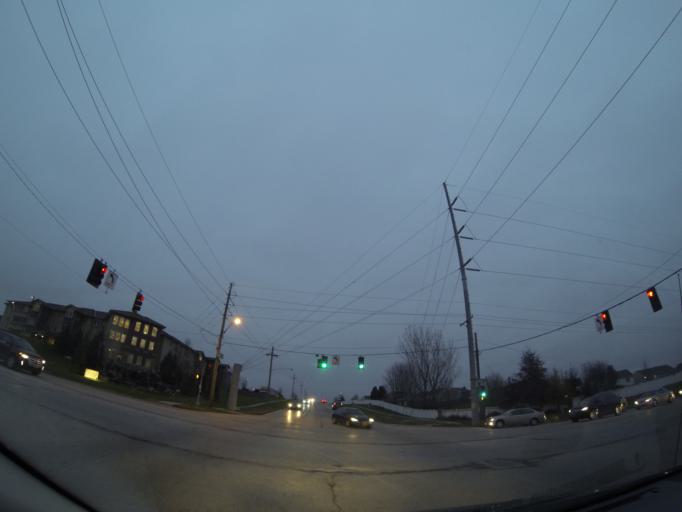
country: US
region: Nebraska
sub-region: Douglas County
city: Elkhorn
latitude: 41.2774
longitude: -96.1772
